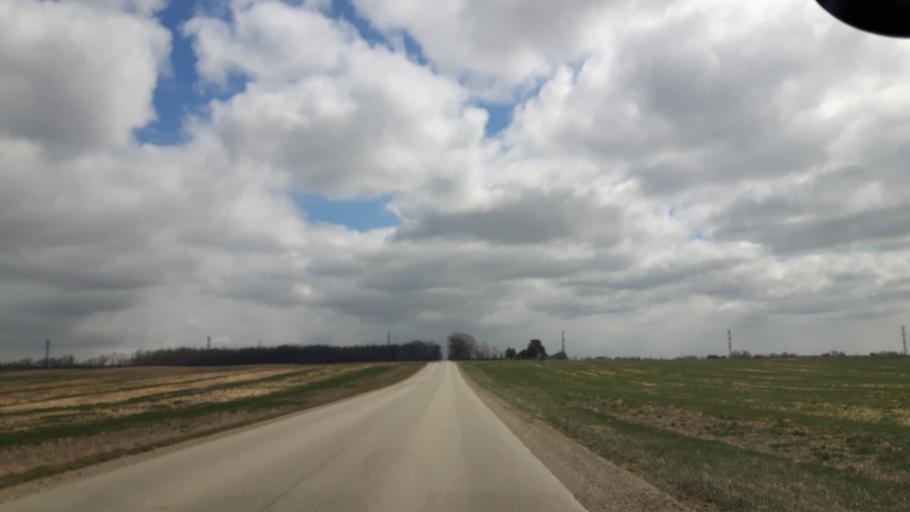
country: CA
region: Ontario
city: Goderich
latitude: 43.6985
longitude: -81.6711
